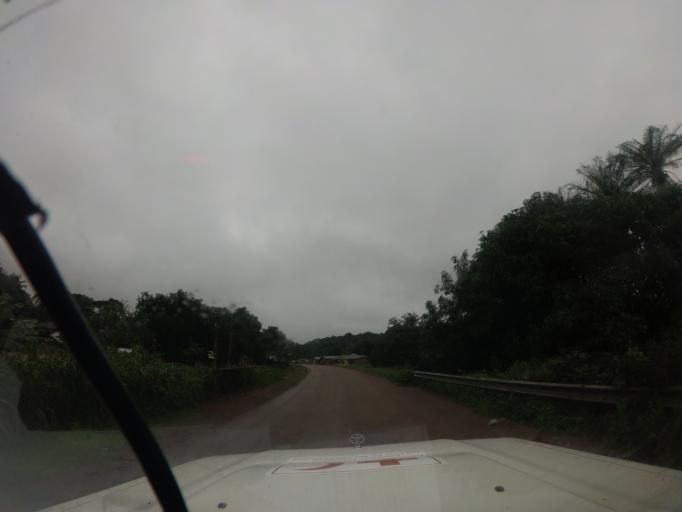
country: SL
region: Northern Province
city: Kabala
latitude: 9.5122
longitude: -11.5911
